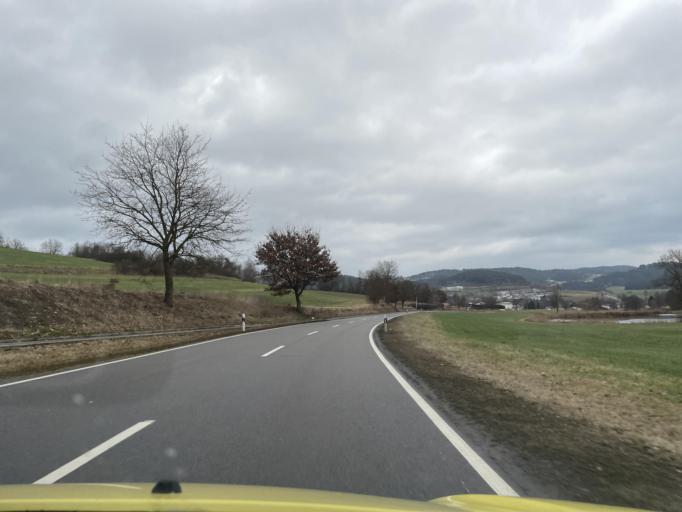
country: DE
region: Bavaria
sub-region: Upper Palatinate
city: Miltach
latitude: 49.1567
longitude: 12.7522
